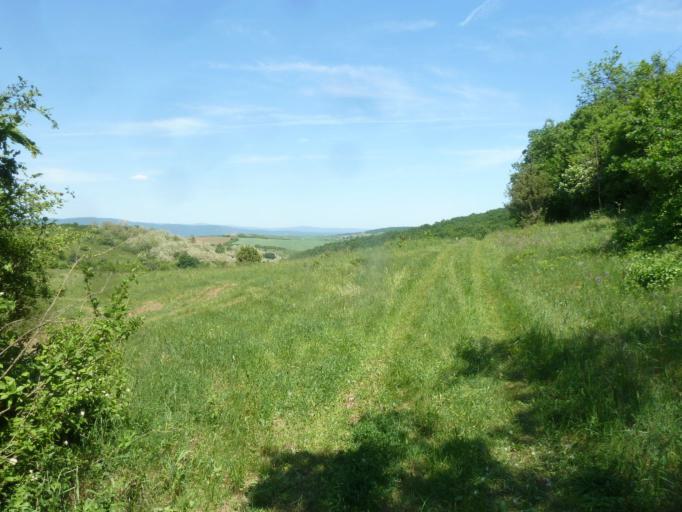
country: HU
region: Borsod-Abauj-Zemplen
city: Szendro
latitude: 48.5341
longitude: 20.8422
